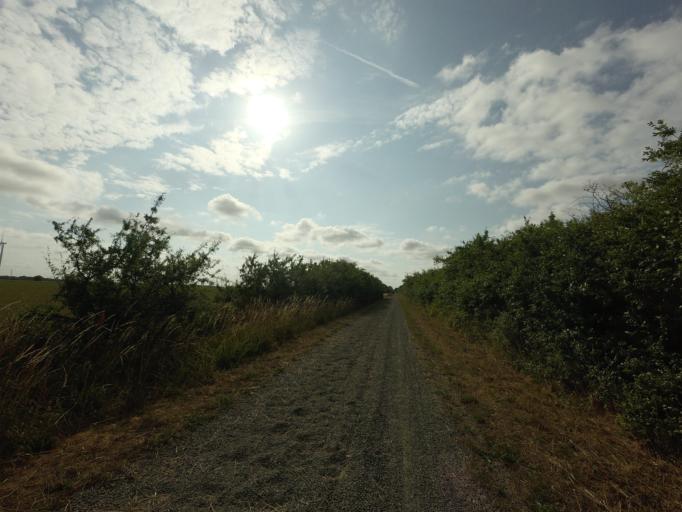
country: SE
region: Skane
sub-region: Helsingborg
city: Odakra
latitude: 56.1599
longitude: 12.7462
